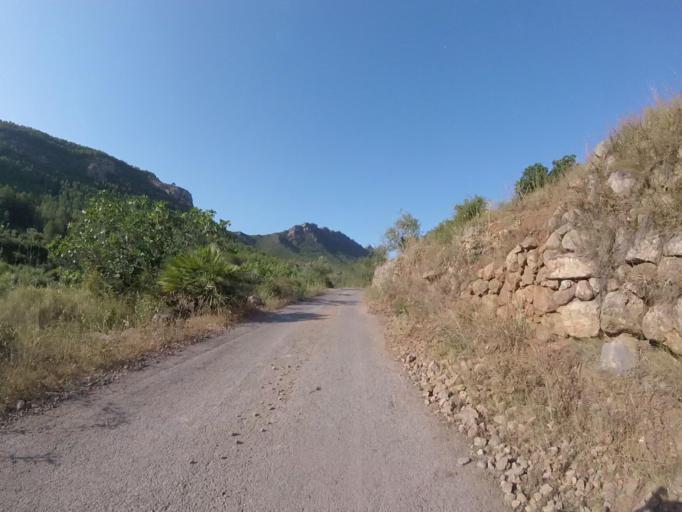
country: ES
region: Valencia
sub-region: Provincia de Castello
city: Benicassim
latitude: 40.0925
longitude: 0.0614
